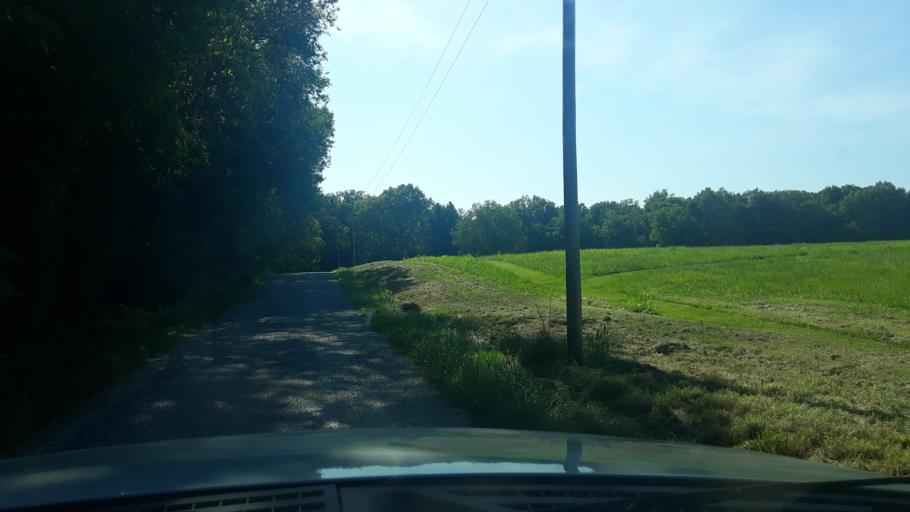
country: US
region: Illinois
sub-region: Saline County
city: Eldorado
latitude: 37.8395
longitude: -88.4914
